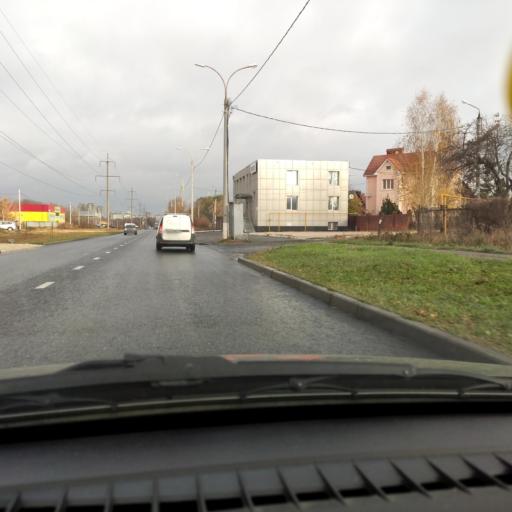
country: RU
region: Samara
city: Tol'yatti
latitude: 53.5194
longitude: 49.3957
